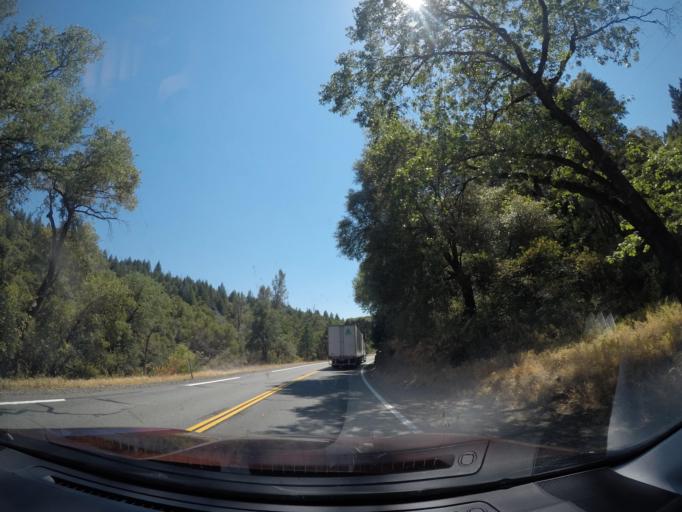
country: US
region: California
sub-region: Shasta County
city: Bella Vista
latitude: 40.7286
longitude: -122.0764
